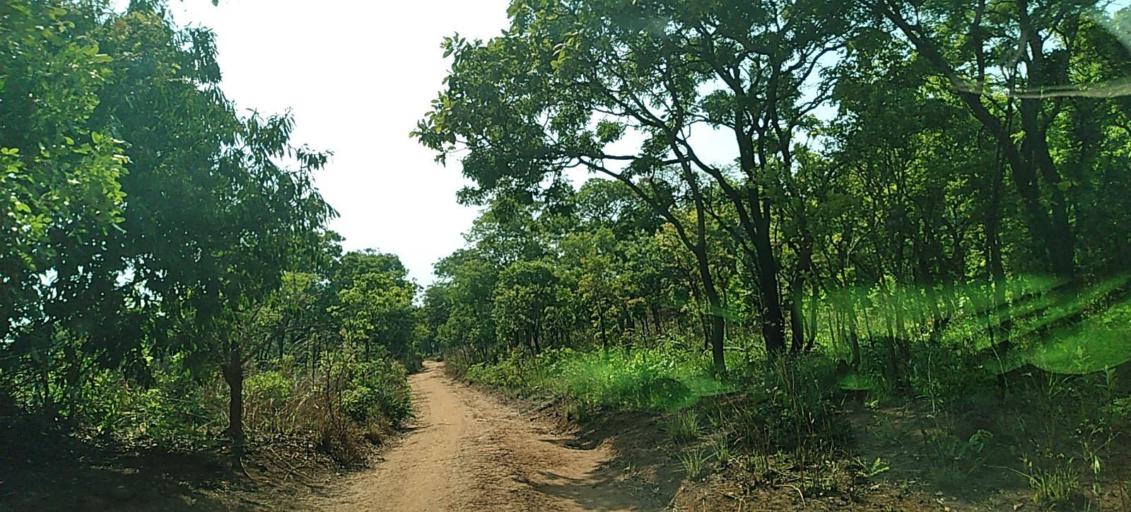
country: ZM
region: North-Western
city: Mwinilunga
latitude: -11.2984
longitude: 24.8651
